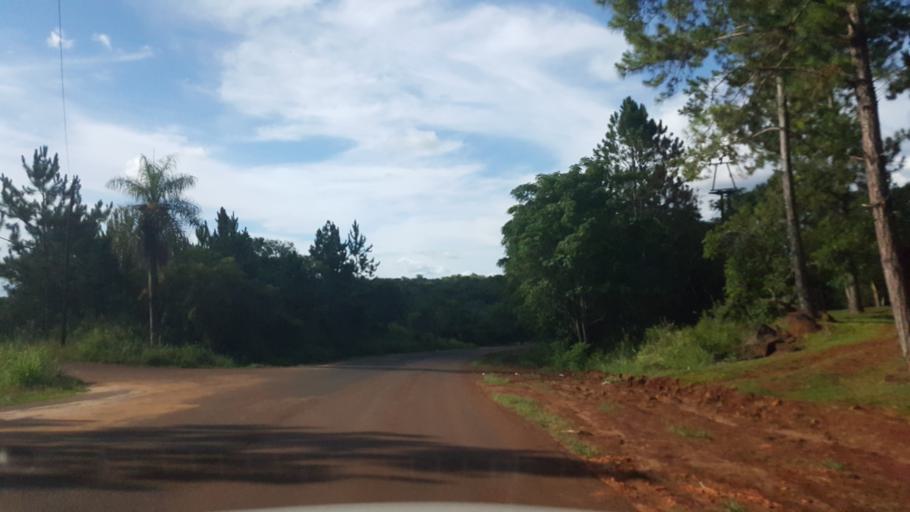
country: AR
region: Misiones
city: Santa Ana
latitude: -27.3620
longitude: -55.5870
